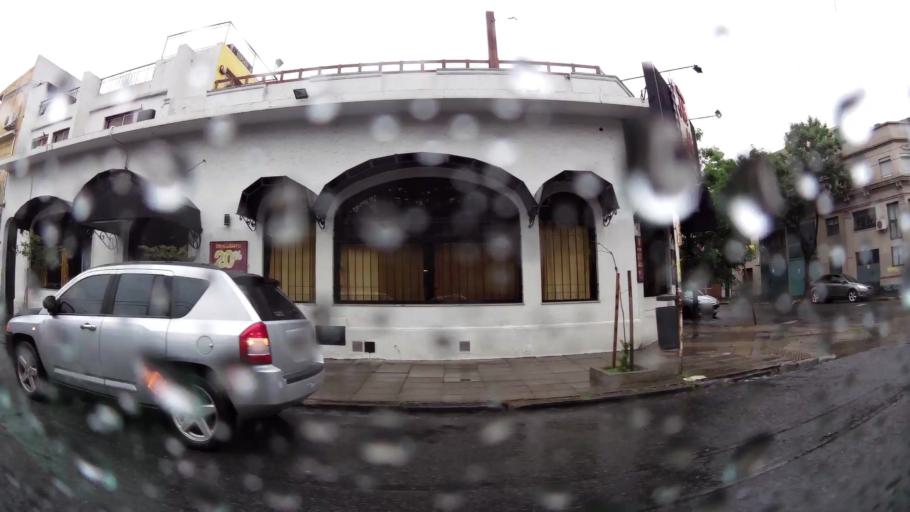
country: AR
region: Buenos Aires F.D.
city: Colegiales
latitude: -34.5950
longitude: -58.4253
